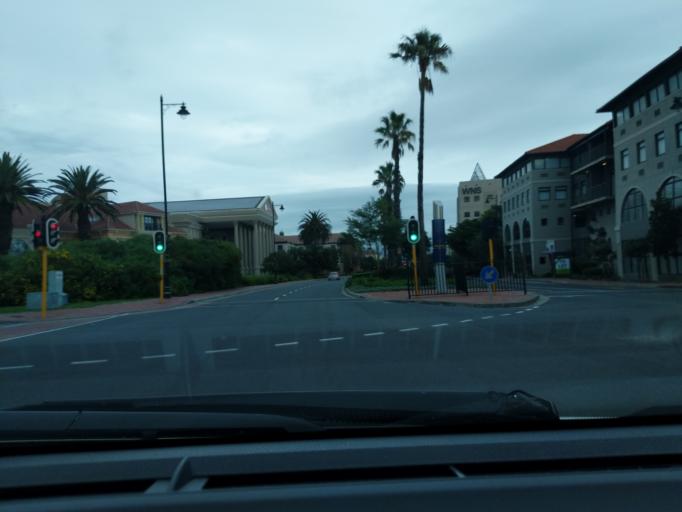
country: ZA
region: Western Cape
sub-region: City of Cape Town
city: Sunset Beach
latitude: -33.8892
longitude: 18.5193
